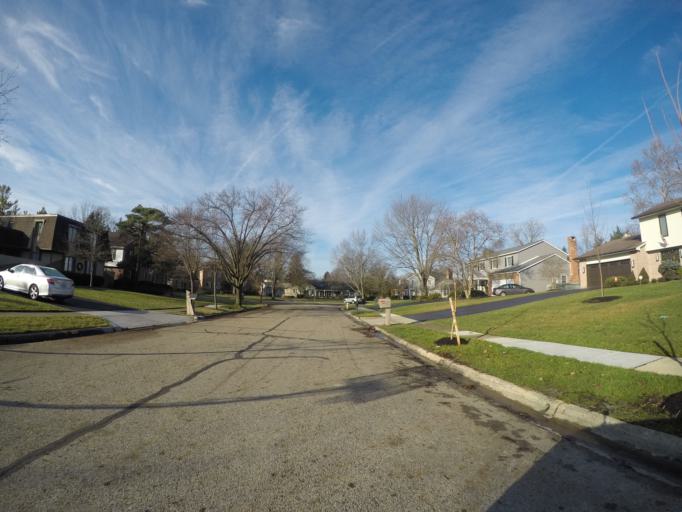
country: US
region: Ohio
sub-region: Franklin County
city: Upper Arlington
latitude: 40.0488
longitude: -83.0840
